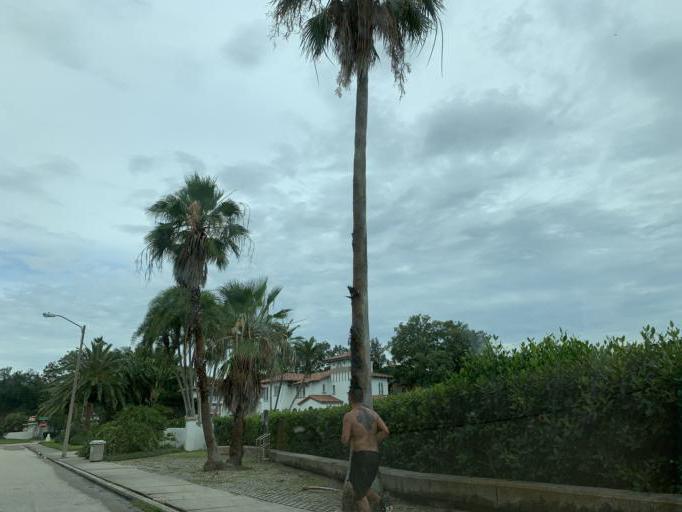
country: US
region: Florida
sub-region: Pinellas County
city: Saint Petersburg
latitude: 27.7925
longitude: -82.6231
